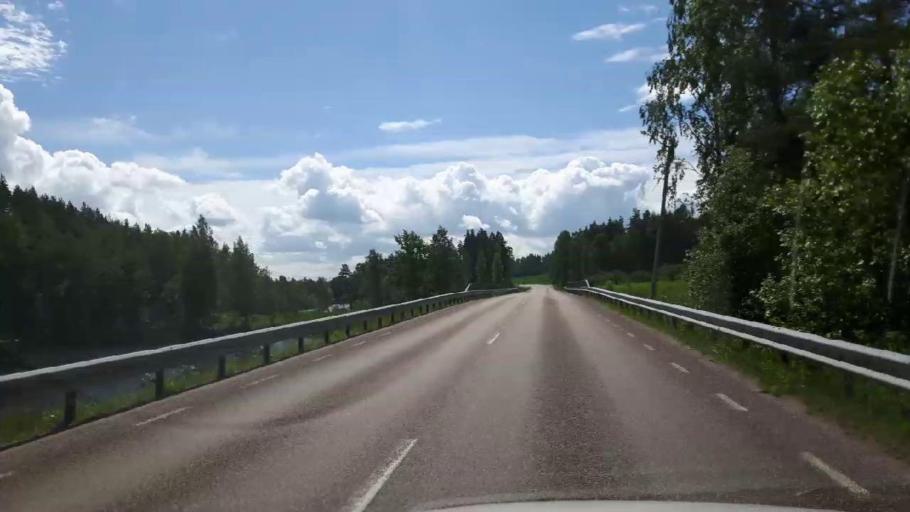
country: SE
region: Dalarna
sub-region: Faluns Kommun
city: Falun
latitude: 60.6321
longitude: 15.7682
